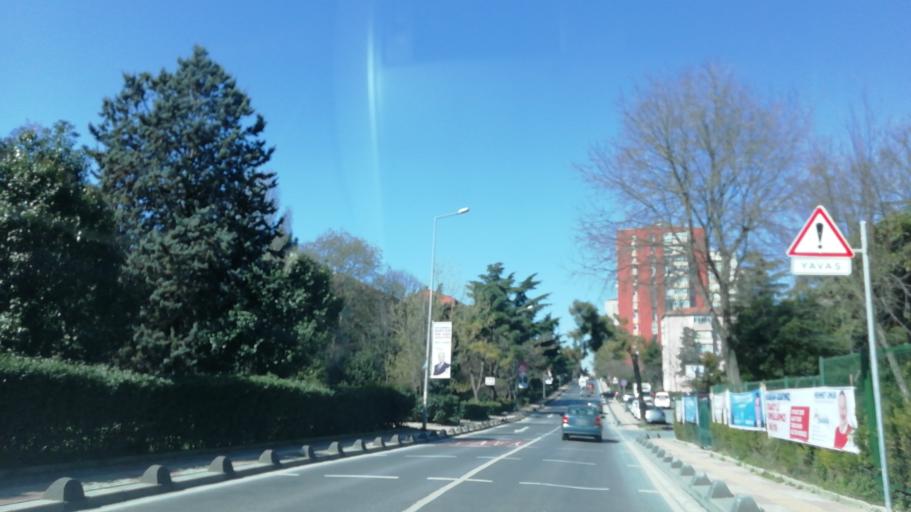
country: TR
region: Istanbul
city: Bahcelievler
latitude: 40.9831
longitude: 28.8650
